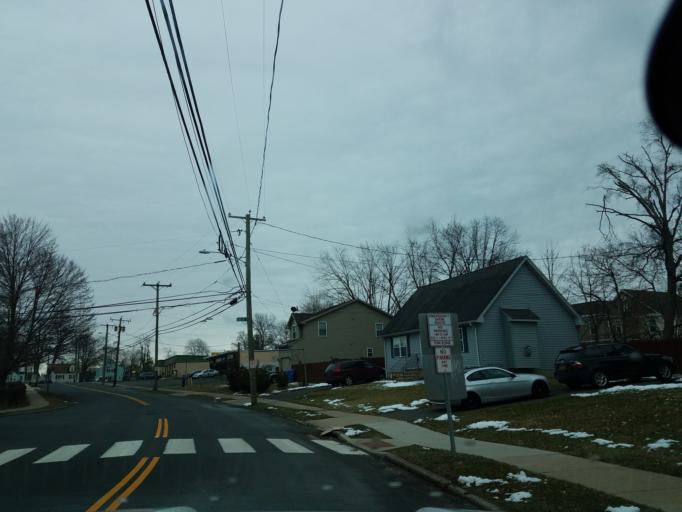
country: US
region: Connecticut
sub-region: Hartford County
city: New Britain
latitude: 41.6941
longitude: -72.7977
